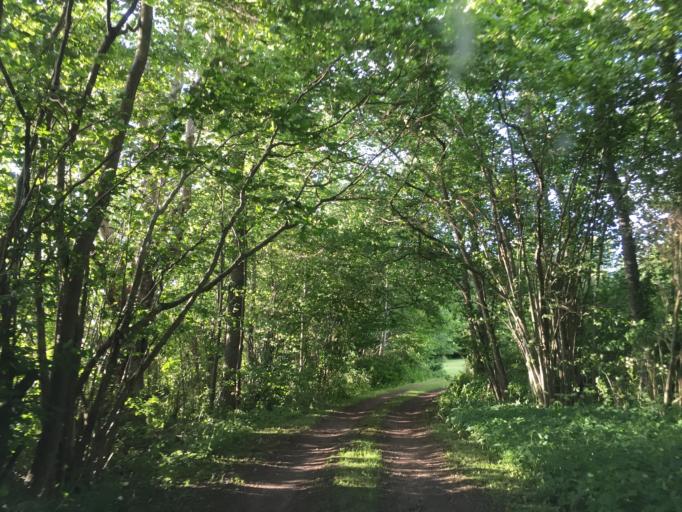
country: SE
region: OEstergoetland
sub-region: Vadstena Kommun
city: Vadstena
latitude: 58.4665
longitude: 14.8389
